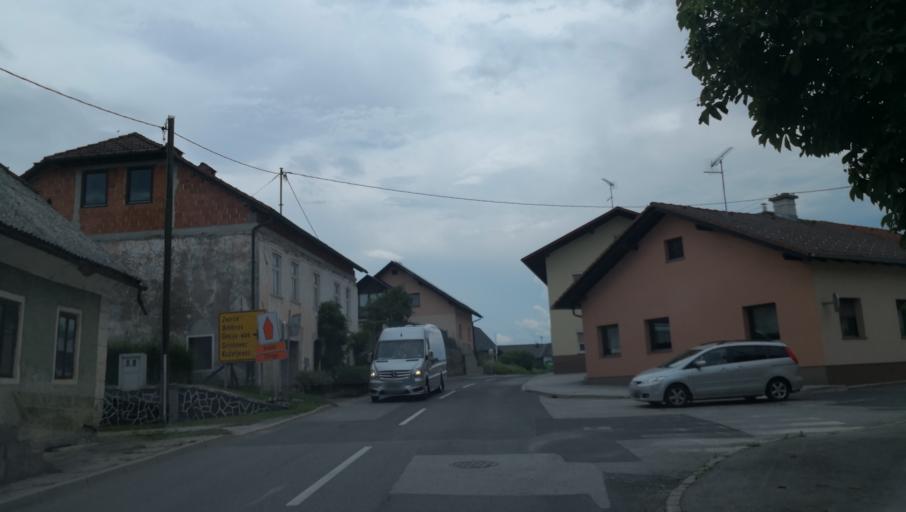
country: SI
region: Ivancna Gorica
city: Ivancna Gorica
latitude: 45.8619
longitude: 14.8316
